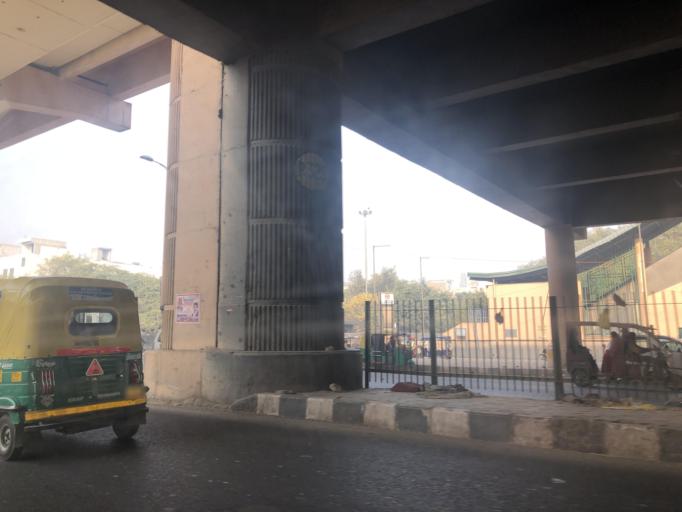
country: IN
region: NCT
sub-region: West Delhi
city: Nangloi Jat
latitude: 28.6810
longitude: 77.0808
